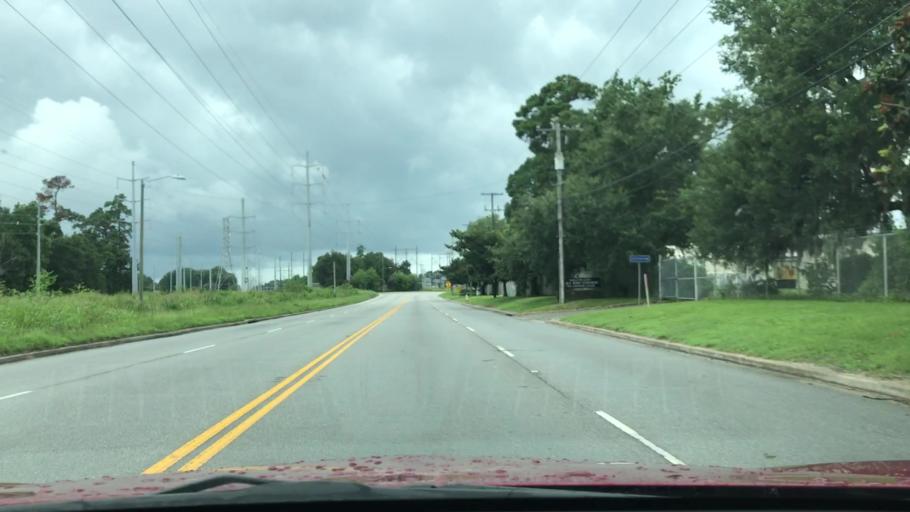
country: US
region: South Carolina
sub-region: Charleston County
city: North Charleston
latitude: 32.8484
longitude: -80.0080
